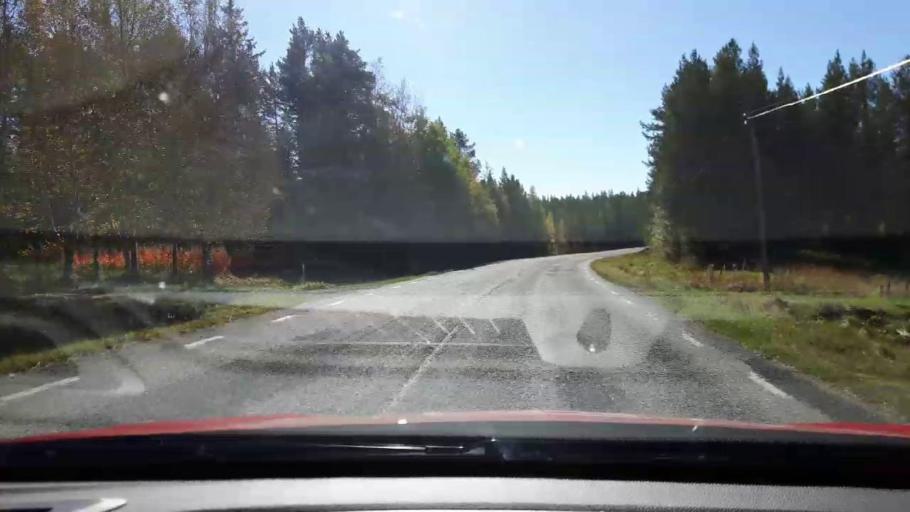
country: SE
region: Jaemtland
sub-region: Harjedalens Kommun
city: Sveg
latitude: 62.3258
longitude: 14.0613
